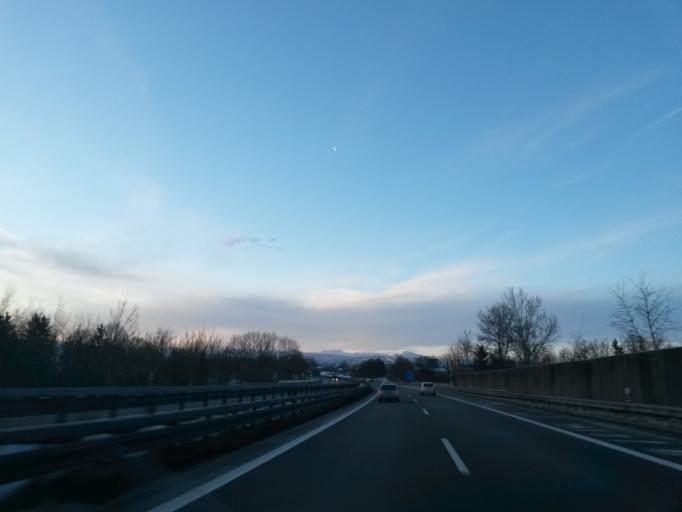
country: DE
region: Bavaria
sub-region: Swabia
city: Lauben
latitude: 47.7692
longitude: 10.3250
